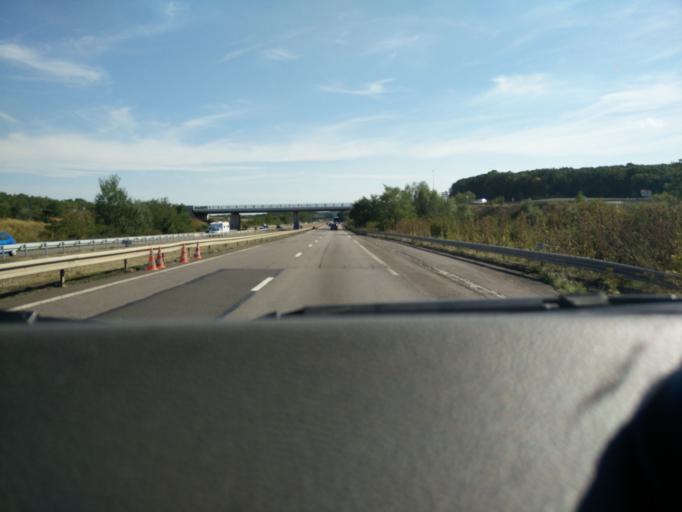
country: FR
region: Lorraine
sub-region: Departement de la Moselle
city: Augny
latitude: 49.0380
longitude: 6.1124
